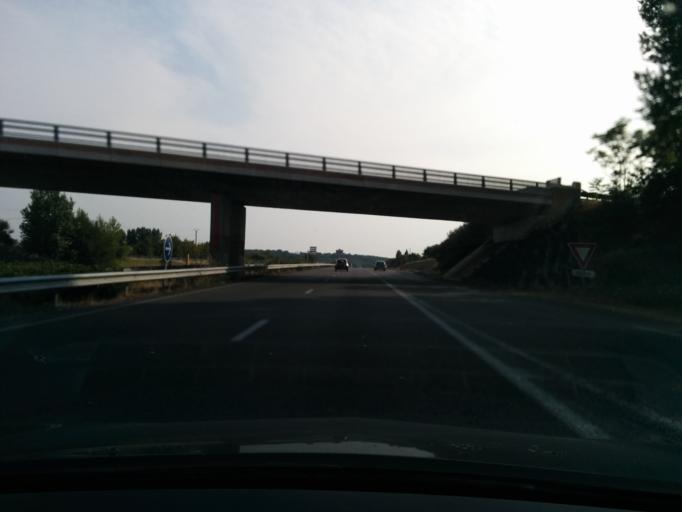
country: FR
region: Midi-Pyrenees
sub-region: Departement du Tarn
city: Saint-Sulpice-la-Pointe
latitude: 43.7592
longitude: 1.7105
